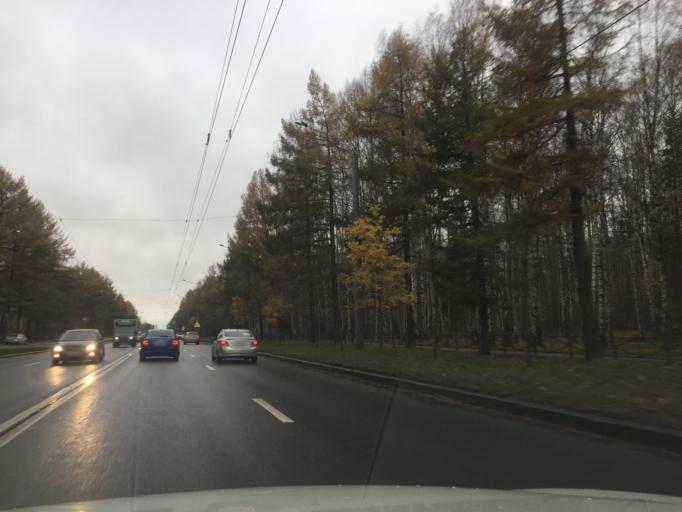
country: RU
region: St.-Petersburg
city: Sosnovka
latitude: 60.0179
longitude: 30.3651
